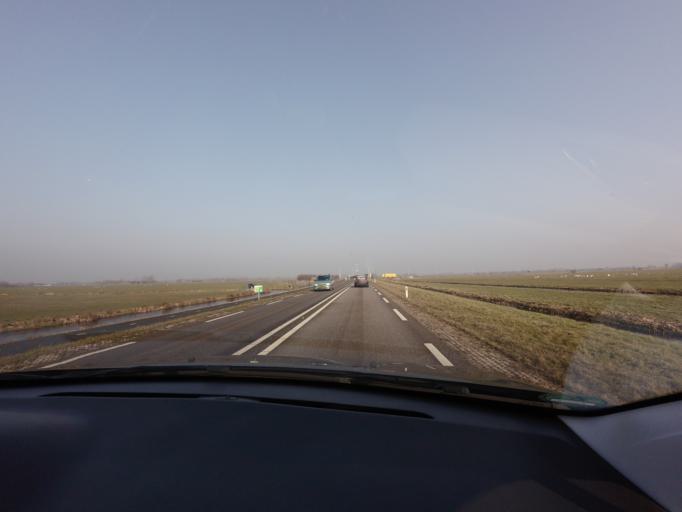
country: NL
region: Utrecht
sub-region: Gemeente Woerden
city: Woerden
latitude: 52.1415
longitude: 4.9118
